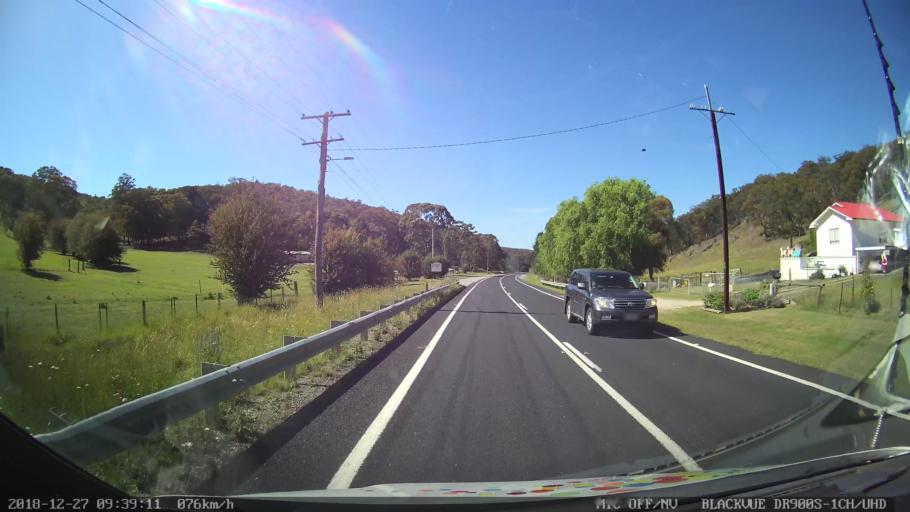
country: AU
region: New South Wales
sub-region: Lithgow
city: Portland
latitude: -33.2901
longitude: 150.0354
